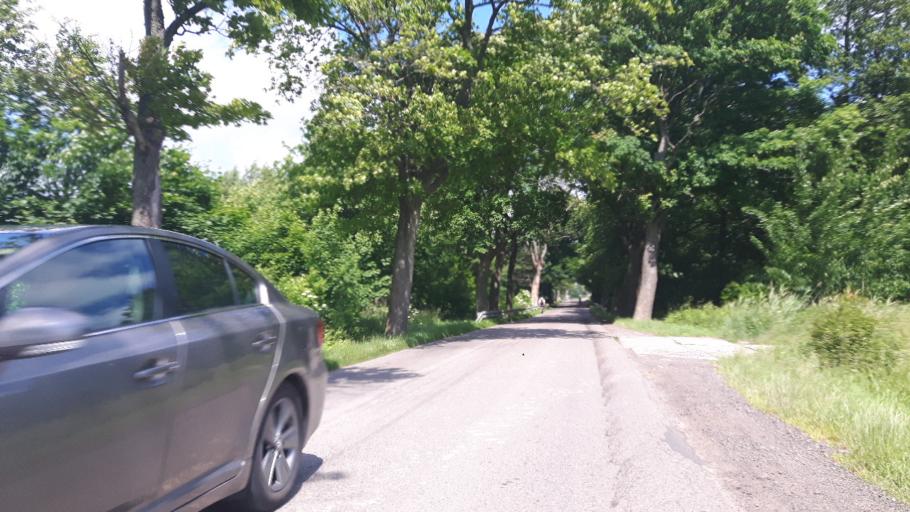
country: PL
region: Pomeranian Voivodeship
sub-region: Powiat slupski
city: Ustka
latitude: 54.5318
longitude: 16.8171
